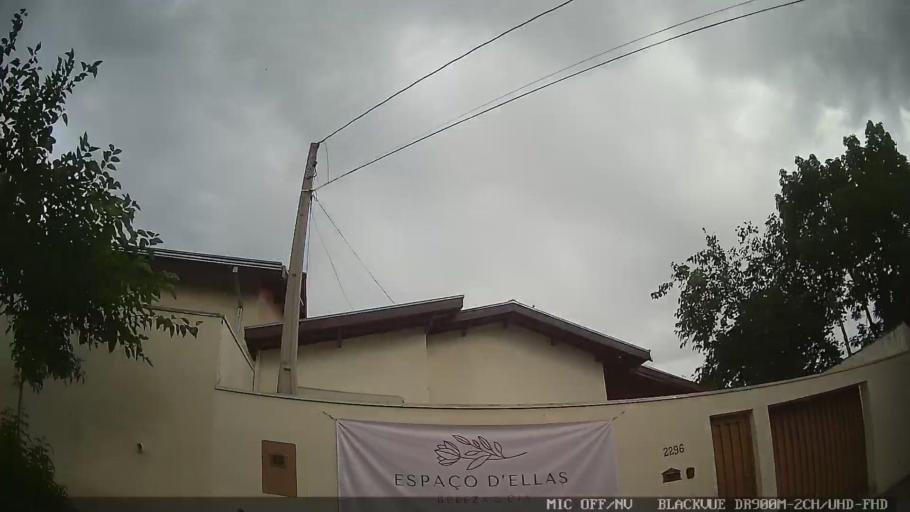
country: BR
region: Sao Paulo
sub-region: Jaguariuna
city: Jaguariuna
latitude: -22.6827
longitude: -46.9850
